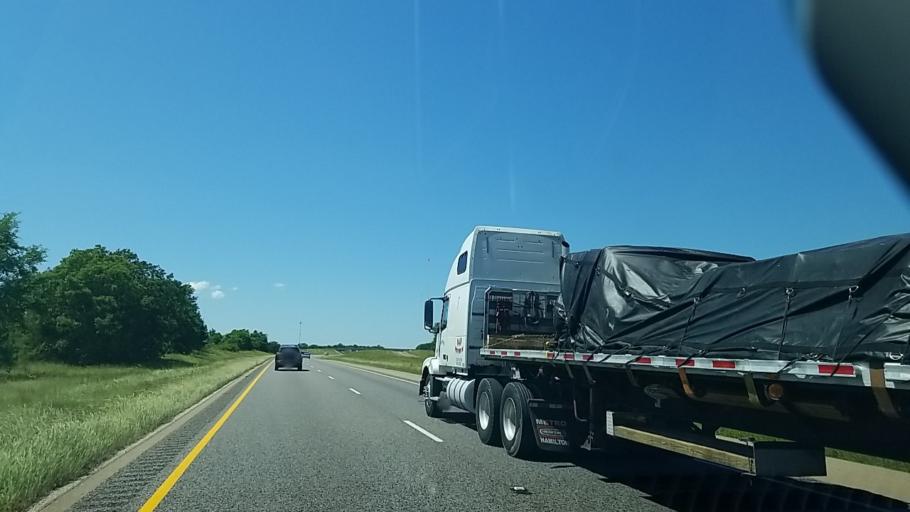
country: US
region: Texas
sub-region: Freestone County
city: Teague
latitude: 31.5792
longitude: -96.1469
